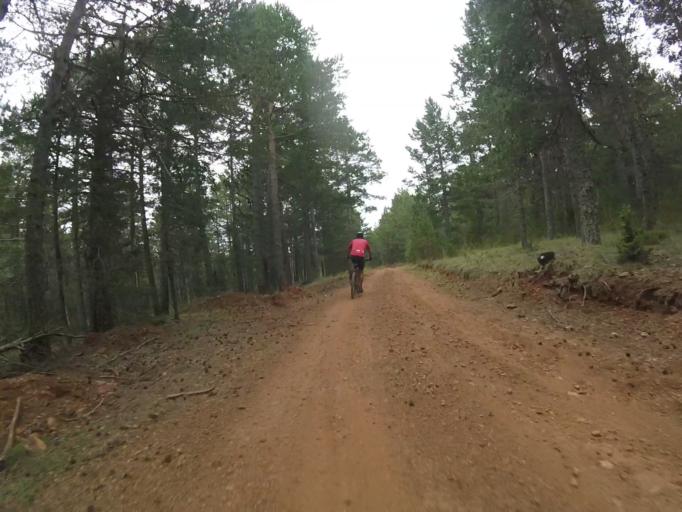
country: ES
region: Aragon
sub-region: Provincia de Teruel
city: Valdelinares
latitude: 40.3614
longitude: -0.6149
